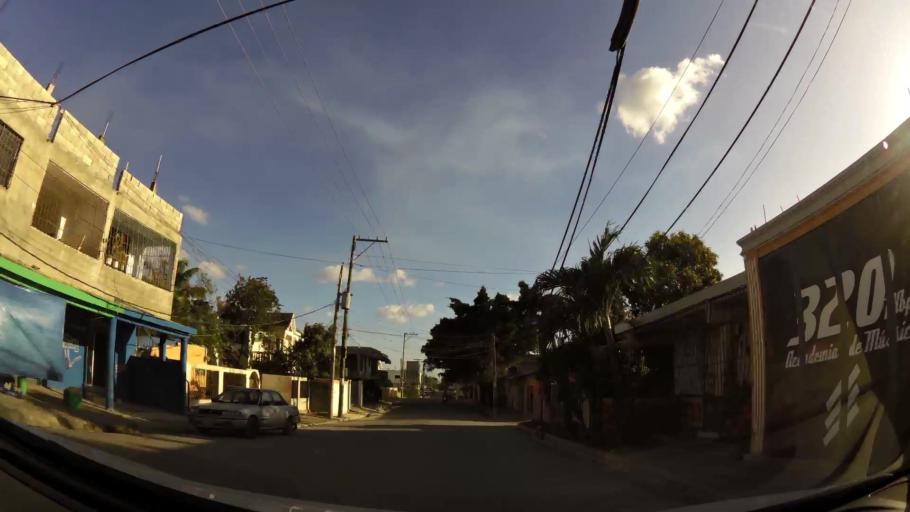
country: DO
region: Santo Domingo
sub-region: Santo Domingo
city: Santo Domingo Este
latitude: 18.4755
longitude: -69.7946
